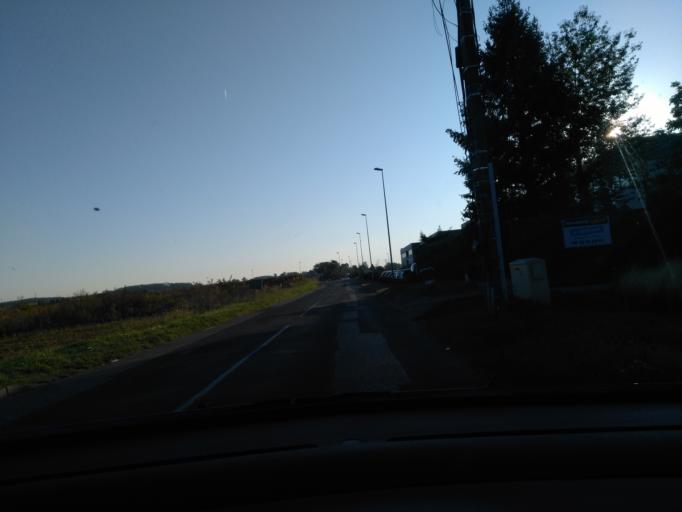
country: FR
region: Rhone-Alpes
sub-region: Departement du Rhone
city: Cailloux-sur-Fontaines
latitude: 45.8567
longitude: 4.8780
